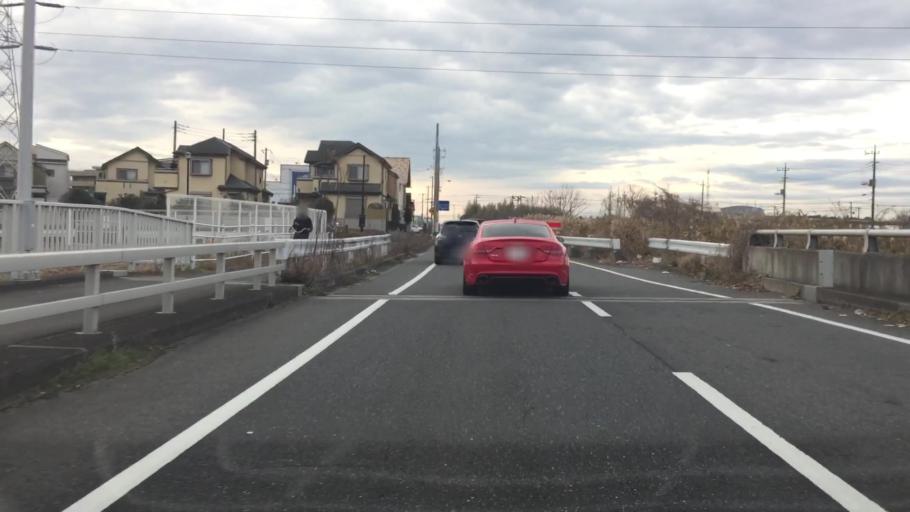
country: JP
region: Chiba
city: Shiroi
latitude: 35.7839
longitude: 140.0059
